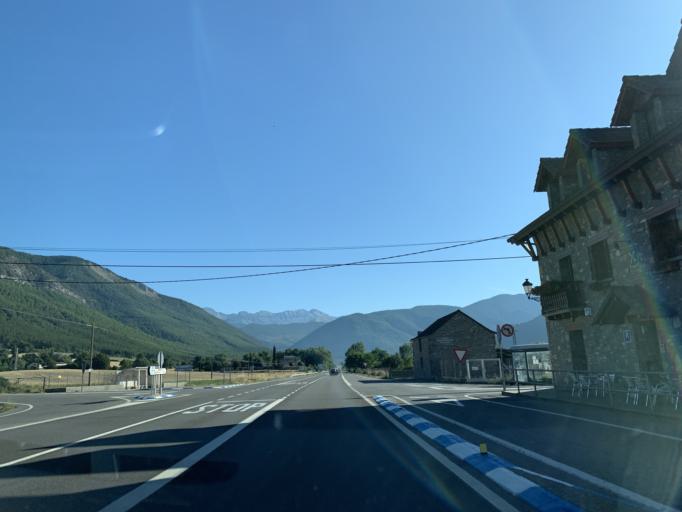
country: ES
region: Aragon
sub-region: Provincia de Huesca
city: Sabinanigo
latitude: 42.5490
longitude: -0.3469
